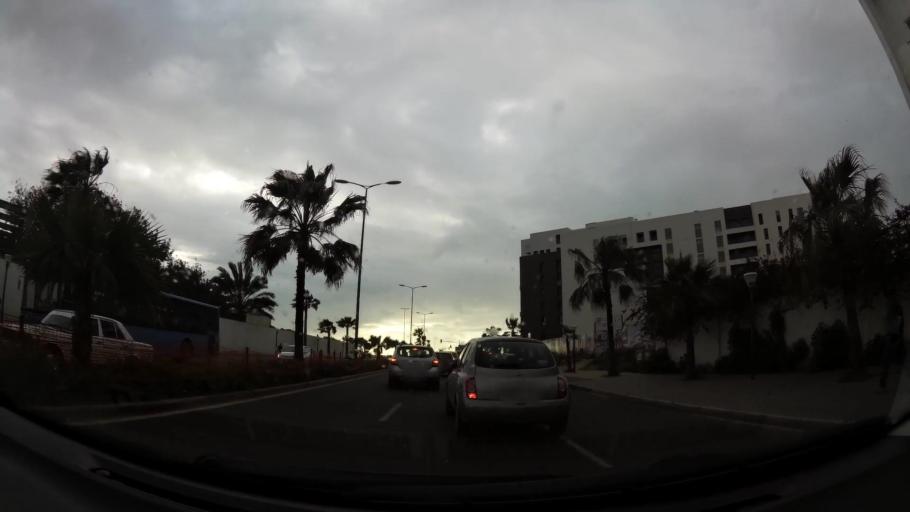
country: MA
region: Grand Casablanca
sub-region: Casablanca
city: Casablanca
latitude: 33.5706
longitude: -7.6986
